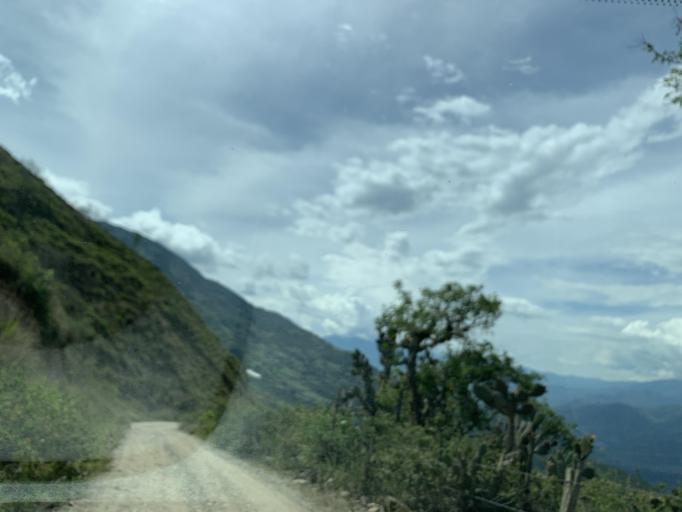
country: CO
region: Boyaca
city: Tipacoque
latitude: 6.4500
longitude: -72.7061
